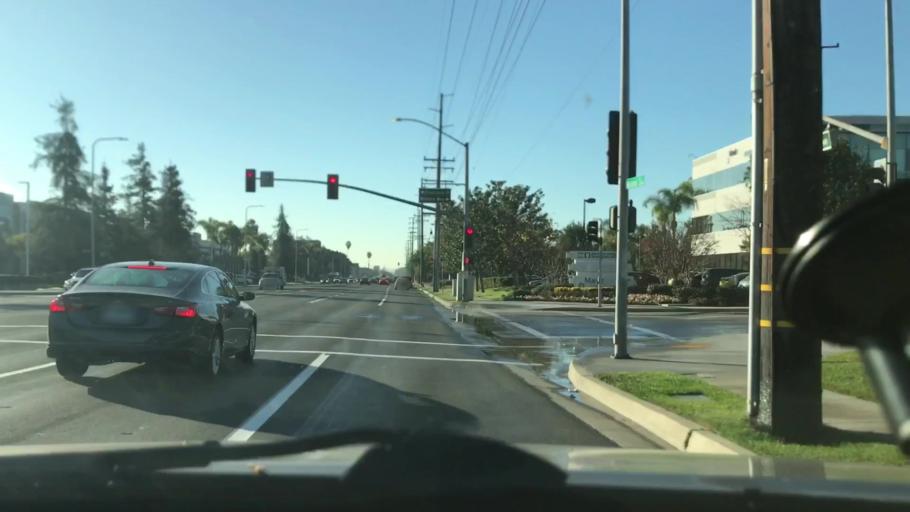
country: US
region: California
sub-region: Los Angeles County
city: West Carson
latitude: 33.8498
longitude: -118.3095
